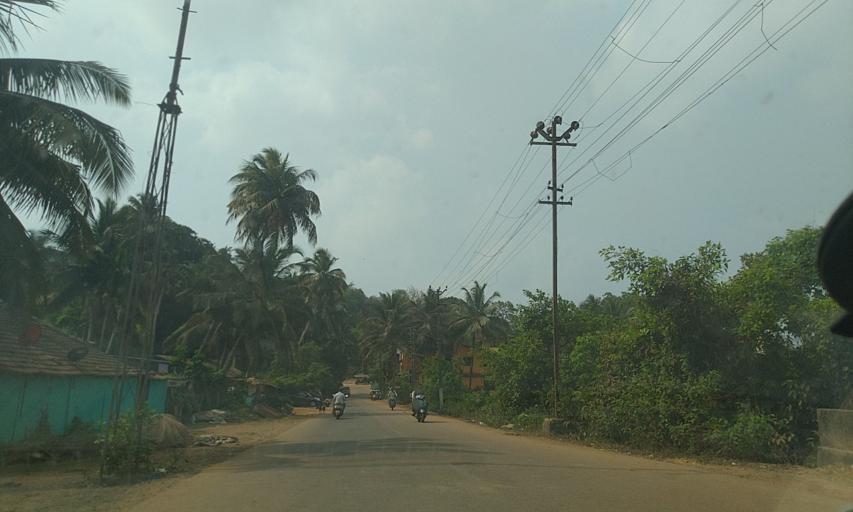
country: IN
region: Goa
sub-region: North Goa
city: Taleigao
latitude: 15.4669
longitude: 73.8276
